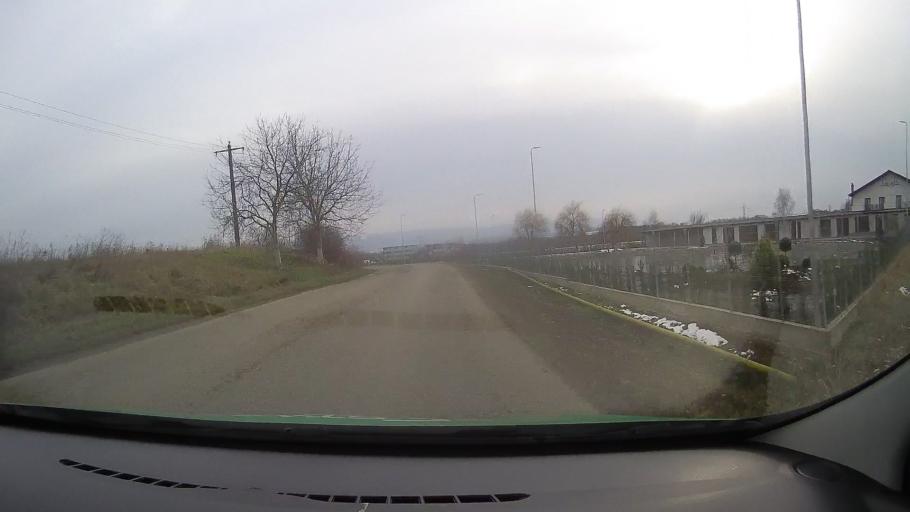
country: RO
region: Hunedoara
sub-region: Comuna Romos
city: Romos
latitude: 45.8772
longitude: 23.2619
